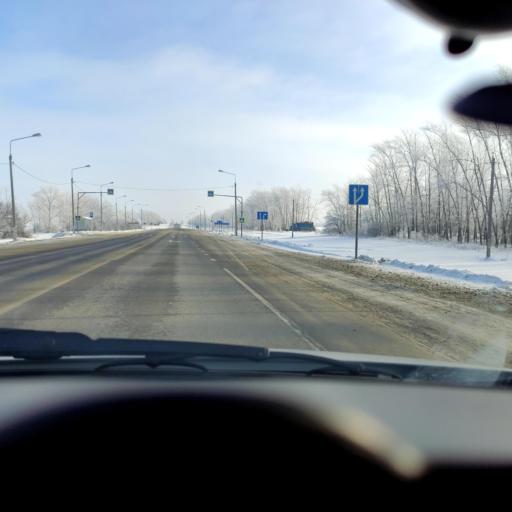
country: RU
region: Kursk
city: Kshenskiy
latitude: 51.6203
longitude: 37.5868
